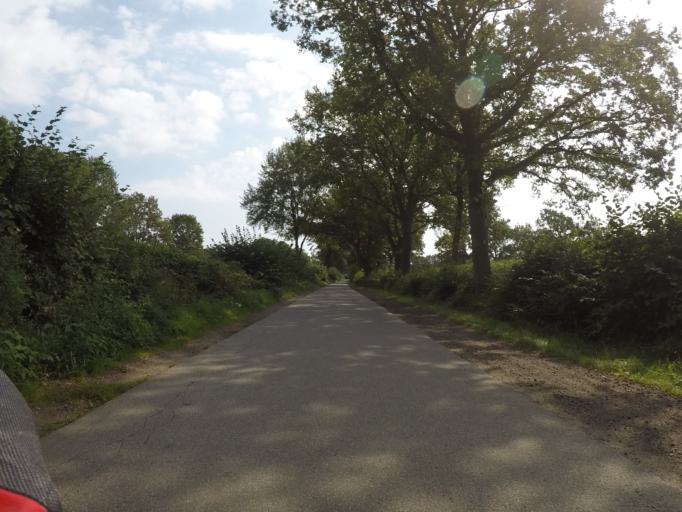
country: DE
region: Schleswig-Holstein
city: Tangstedt
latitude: 53.7575
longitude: 10.0355
